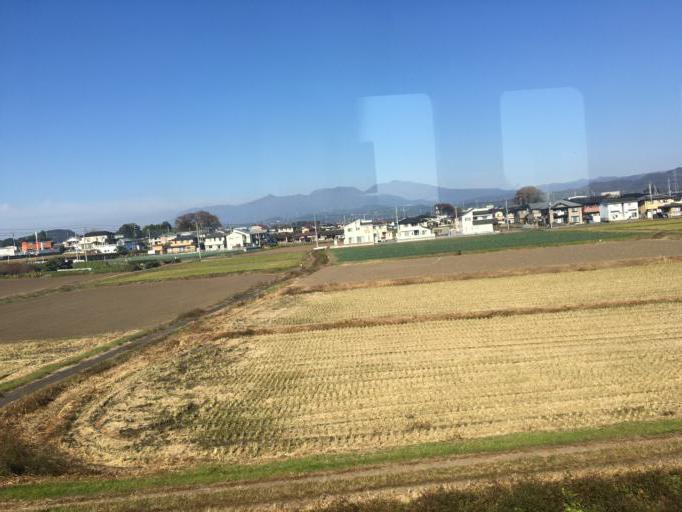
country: JP
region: Gunma
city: Kiryu
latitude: 36.3978
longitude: 139.3000
